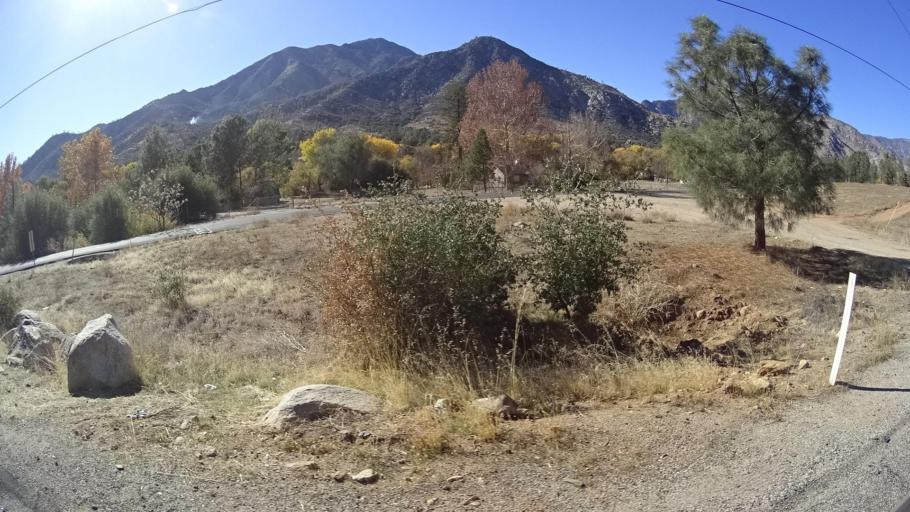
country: US
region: California
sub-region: Kern County
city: Kernville
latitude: 35.7704
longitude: -118.4302
